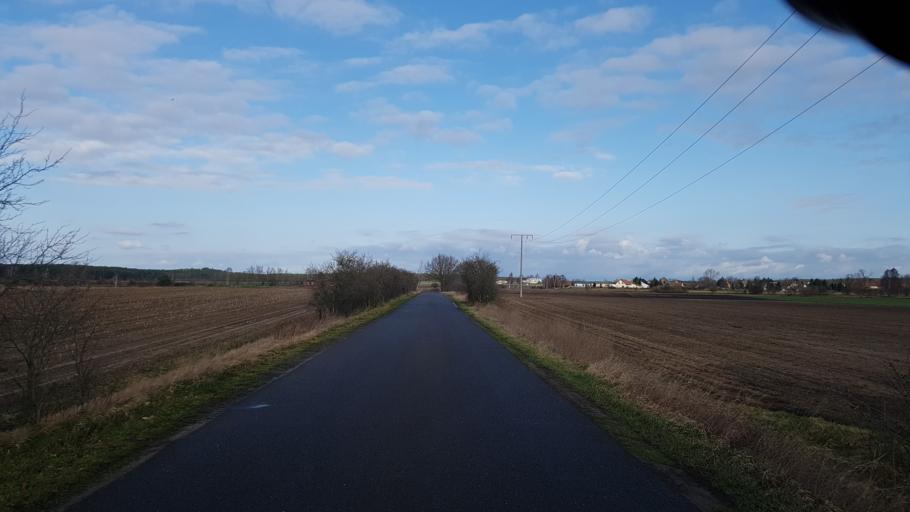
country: DE
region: Brandenburg
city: Schlieben
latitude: 51.7155
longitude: 13.3129
